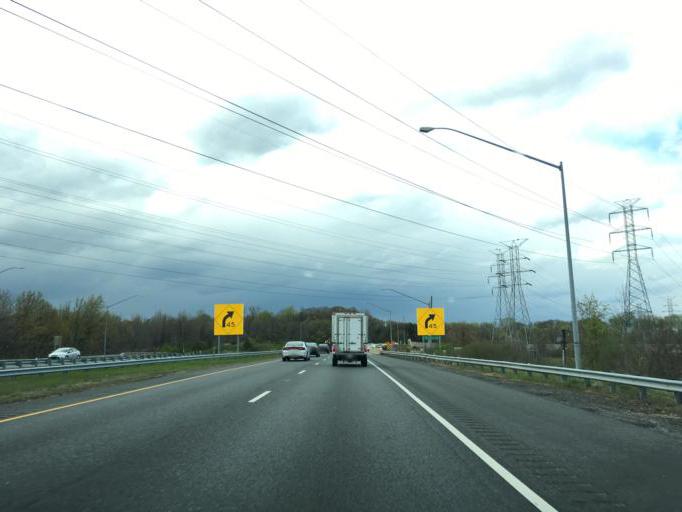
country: US
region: Maryland
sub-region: Baltimore County
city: Rosedale
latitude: 39.3093
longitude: -76.5017
